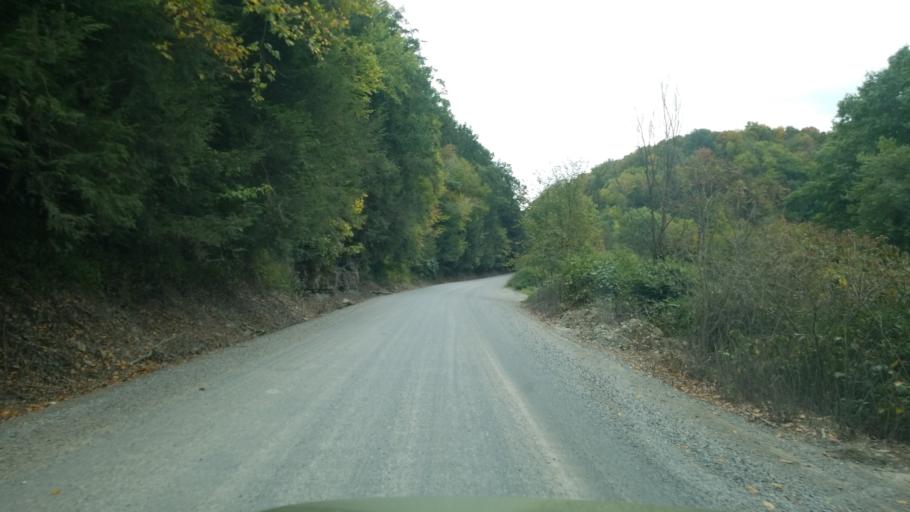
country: US
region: Pennsylvania
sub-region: Clearfield County
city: Curwensville
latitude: 40.9672
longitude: -78.4889
